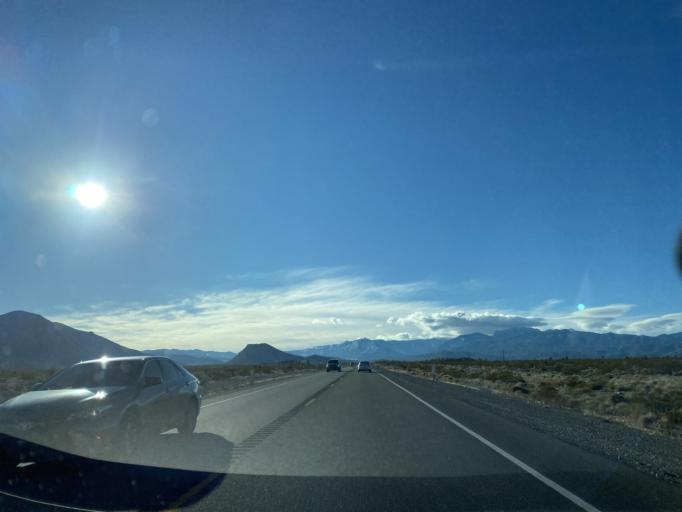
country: US
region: Nevada
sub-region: Clark County
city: Summerlin South
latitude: 36.3191
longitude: -115.3618
